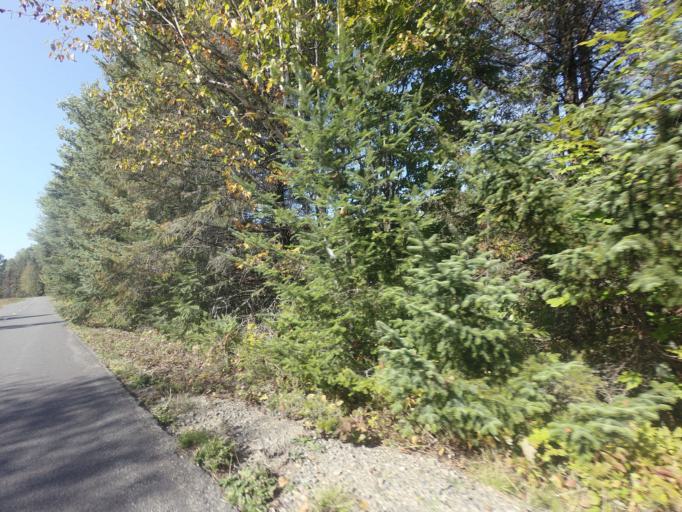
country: CA
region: Quebec
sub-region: Laurentides
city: Mont-Tremblant
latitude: 46.1262
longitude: -74.5300
